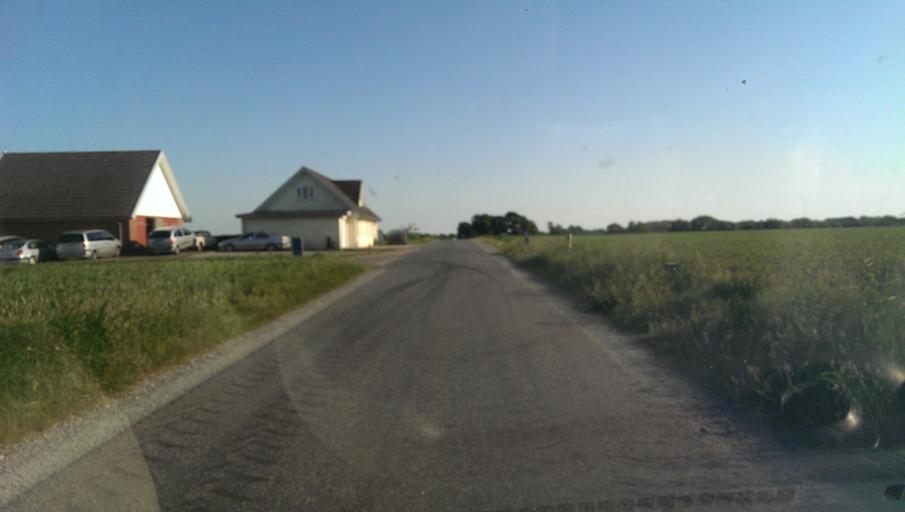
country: DK
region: South Denmark
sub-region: Esbjerg Kommune
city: Bramming
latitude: 55.5341
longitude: 8.6602
